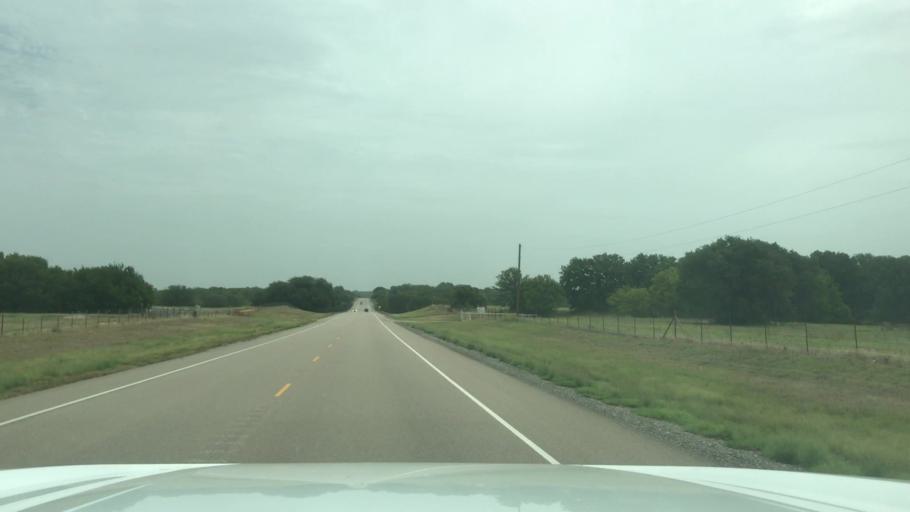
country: US
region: Texas
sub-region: Hamilton County
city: Hico
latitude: 31.9779
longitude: -97.9023
